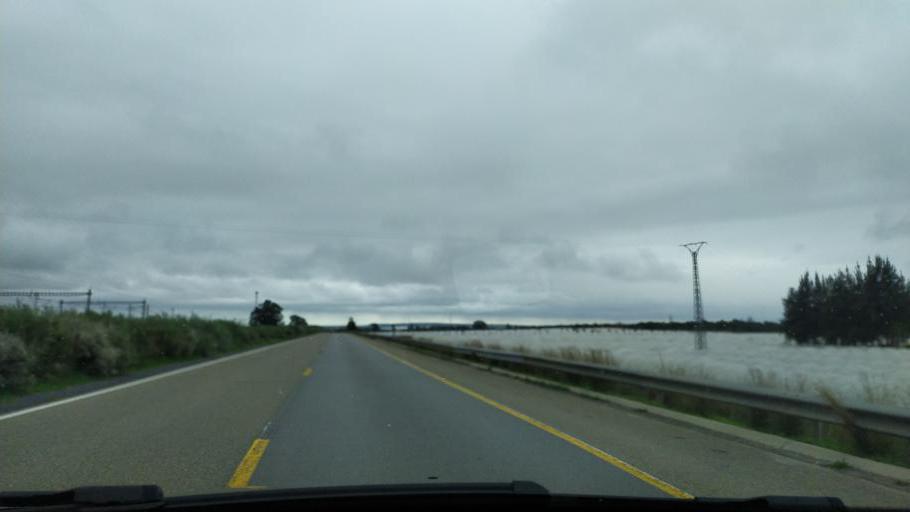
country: MA
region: Gharb-Chrarda-Beni Hssen
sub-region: Kenitra Province
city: Lalla Mimouna
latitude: 34.8954
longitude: -6.2094
